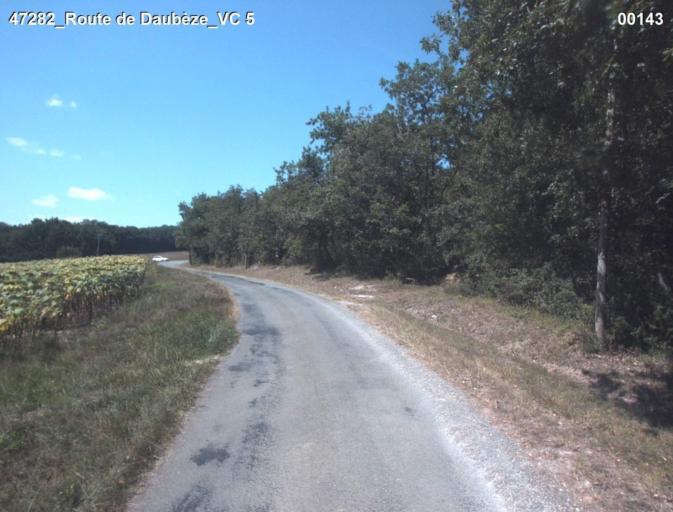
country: FR
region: Aquitaine
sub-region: Departement du Lot-et-Garonne
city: Laplume
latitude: 44.0853
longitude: 0.5331
